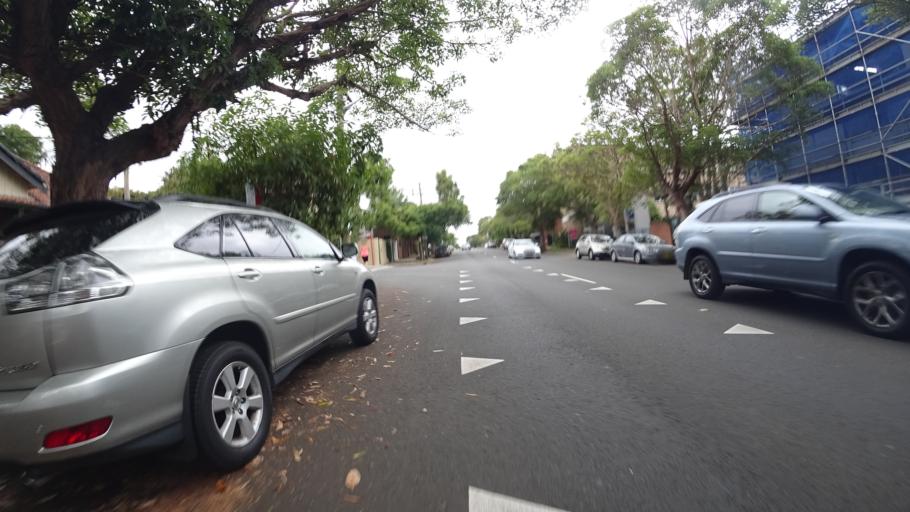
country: AU
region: New South Wales
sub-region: North Sydney
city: Crows Nest
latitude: -33.8278
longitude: 151.2065
